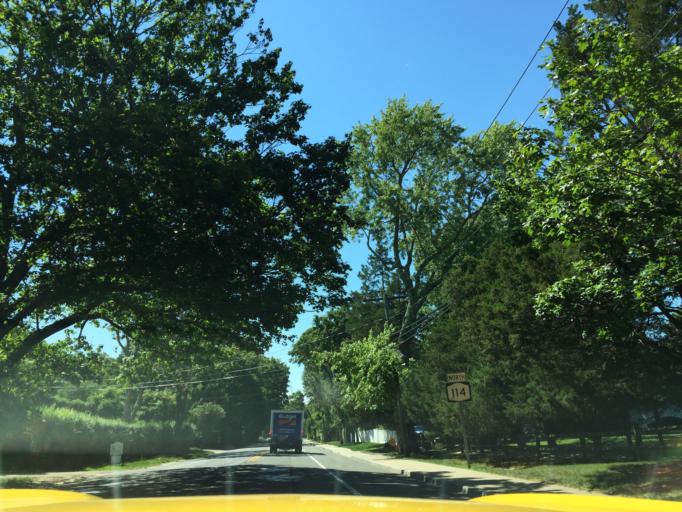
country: US
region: New York
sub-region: Suffolk County
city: Sag Harbor
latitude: 40.9950
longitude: -72.2808
